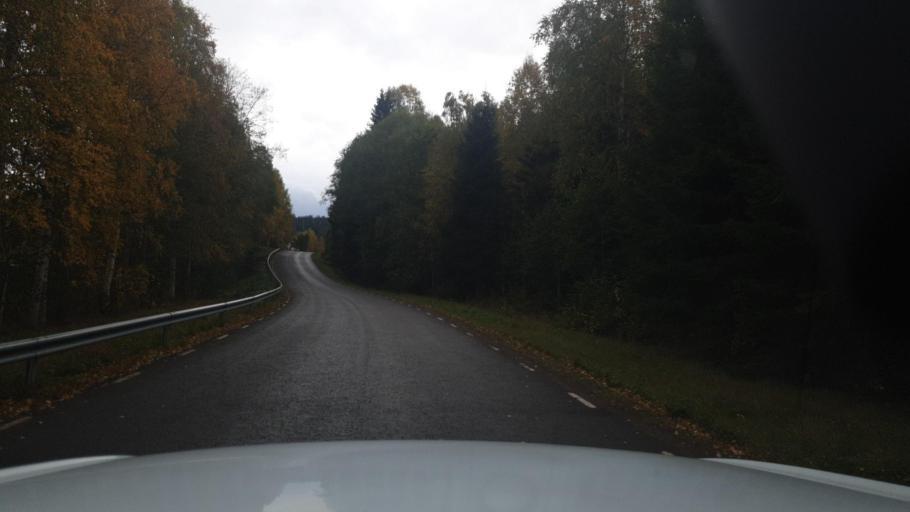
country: SE
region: Vaermland
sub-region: Eda Kommun
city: Charlottenberg
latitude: 60.0233
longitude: 12.6176
